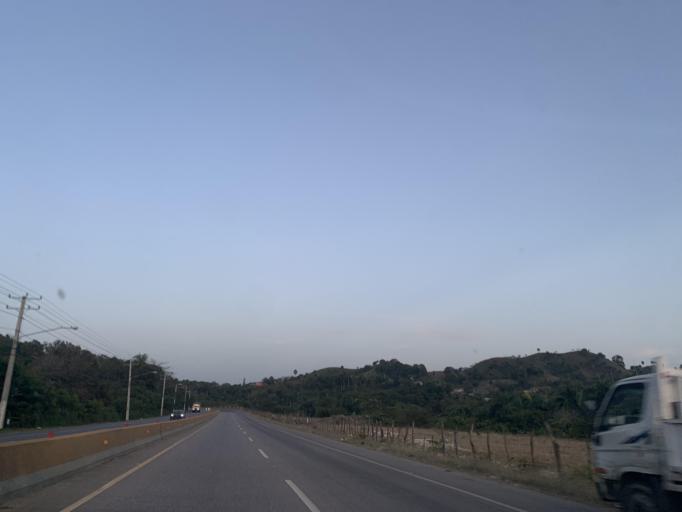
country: DO
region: Puerto Plata
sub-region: Puerto Plata
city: Puerto Plata
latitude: 19.8225
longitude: -70.7420
